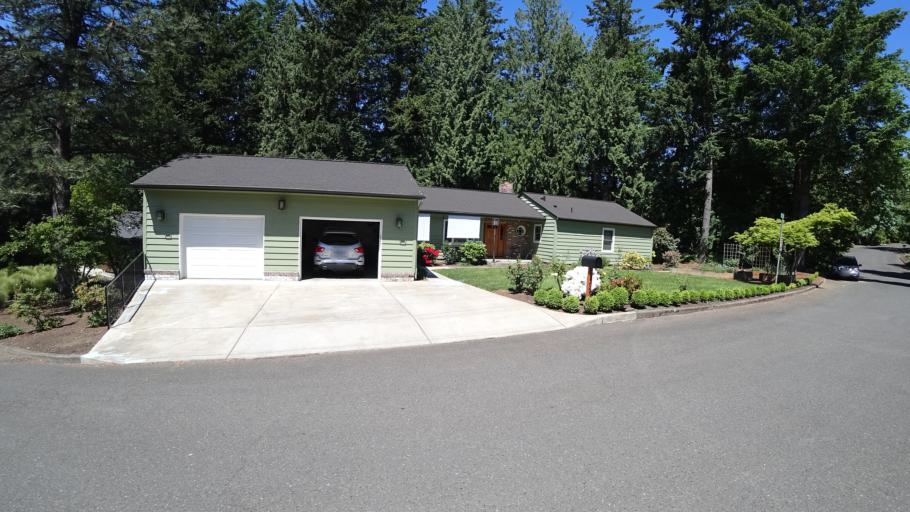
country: US
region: Oregon
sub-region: Washington County
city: Raleigh Hills
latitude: 45.4890
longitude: -122.7149
